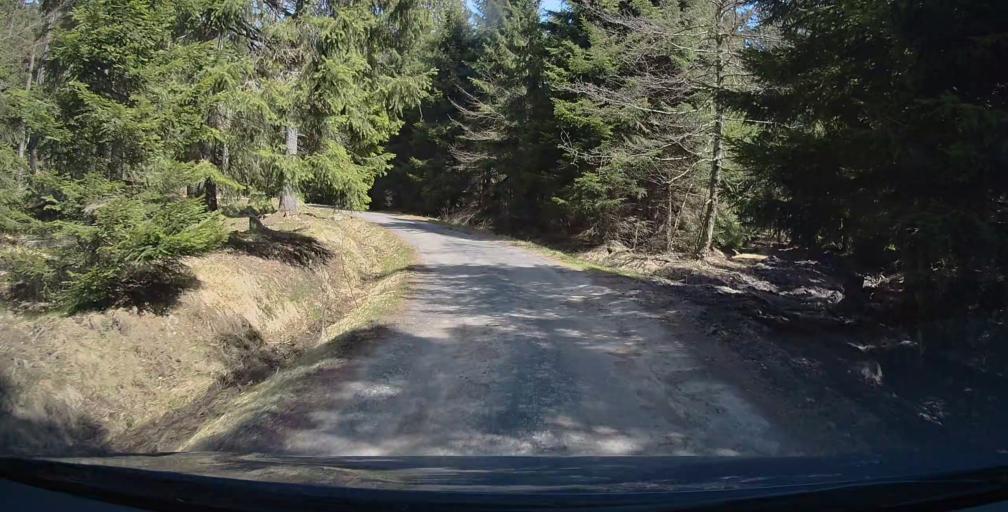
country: CZ
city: Machov
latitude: 50.4661
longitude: 16.2953
